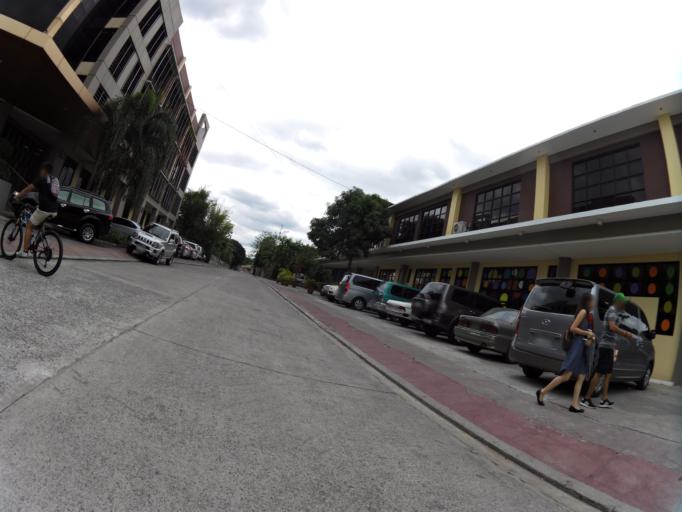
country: PH
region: Calabarzon
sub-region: Province of Rizal
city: Antipolo
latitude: 14.6376
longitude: 121.1112
